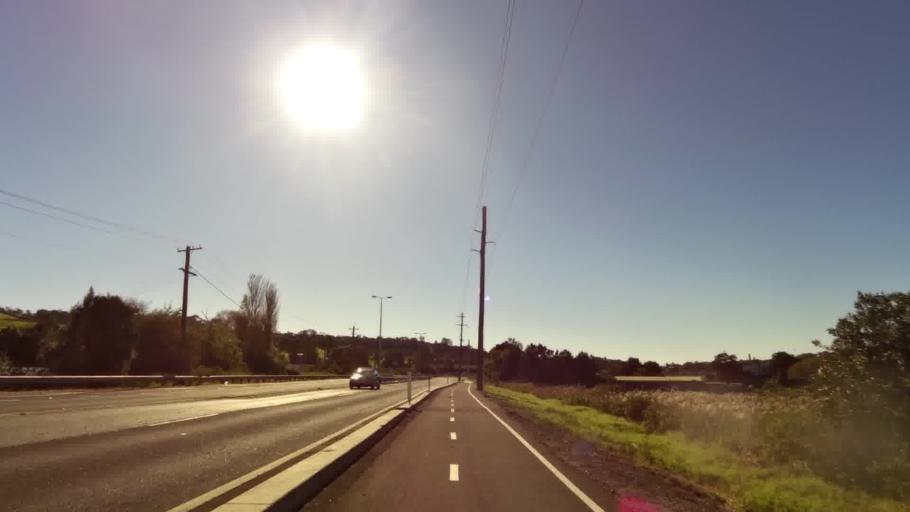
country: AU
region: New South Wales
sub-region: Wollongong
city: Koonawarra
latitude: -34.4720
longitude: 150.8163
